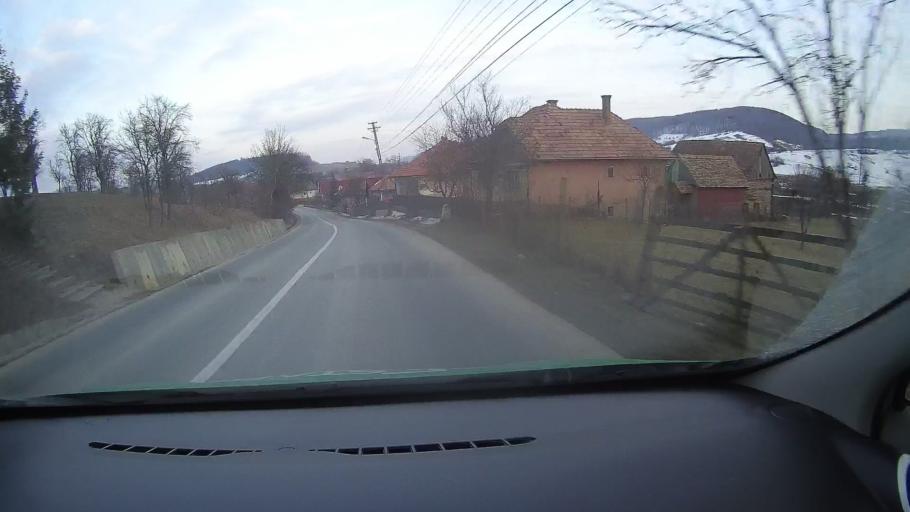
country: RO
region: Harghita
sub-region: Comuna Lupeni
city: Lupeni
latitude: 46.3599
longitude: 25.1733
